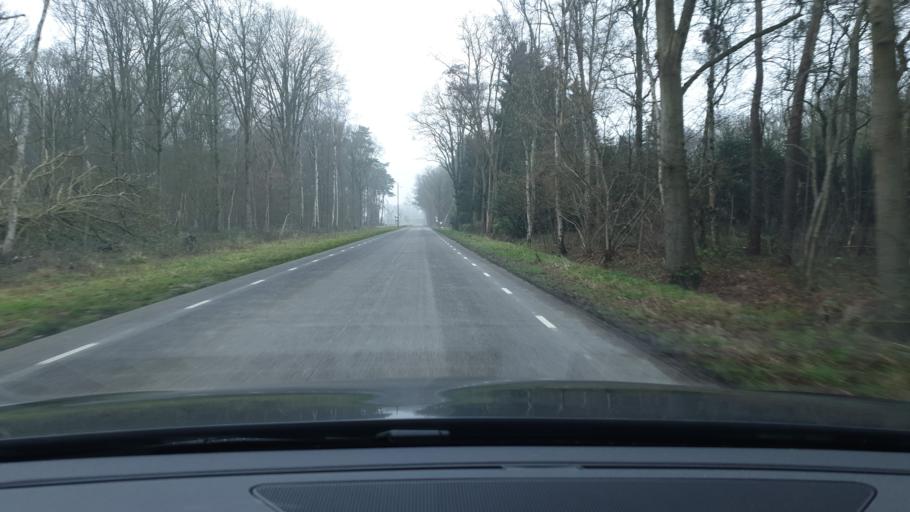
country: NL
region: North Brabant
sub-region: Gemeente Eindhoven
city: Meerhoven
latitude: 51.4633
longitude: 5.4008
